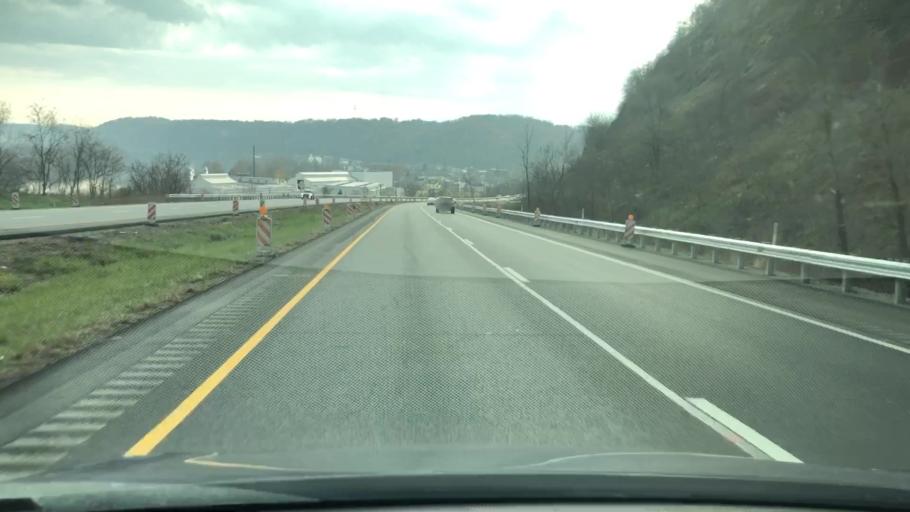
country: US
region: Pennsylvania
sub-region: Allegheny County
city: Tarentum
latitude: 40.5942
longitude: -79.7715
